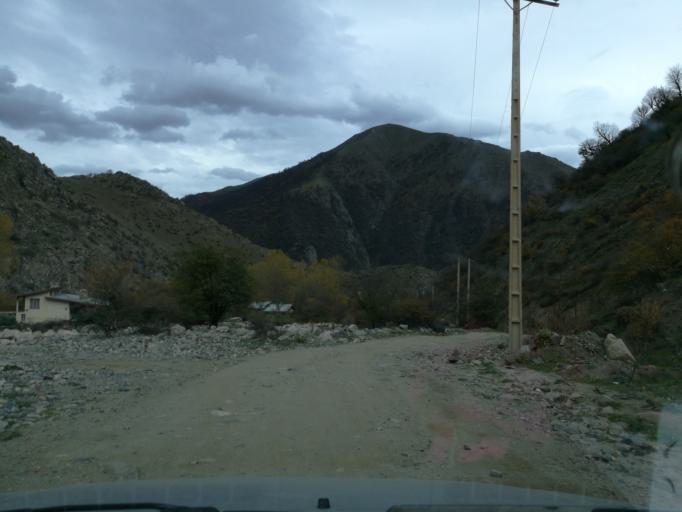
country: IR
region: Mazandaran
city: `Abbasabad
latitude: 36.4389
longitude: 51.0514
